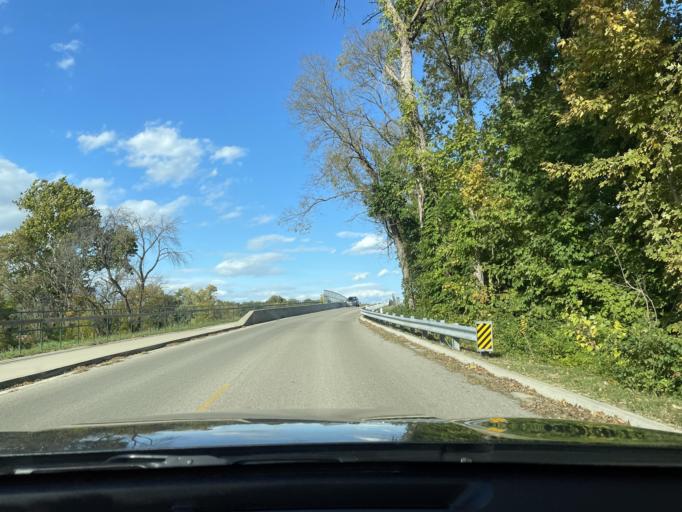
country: US
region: Missouri
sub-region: Buchanan County
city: Saint Joseph
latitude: 39.7350
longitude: -94.8381
